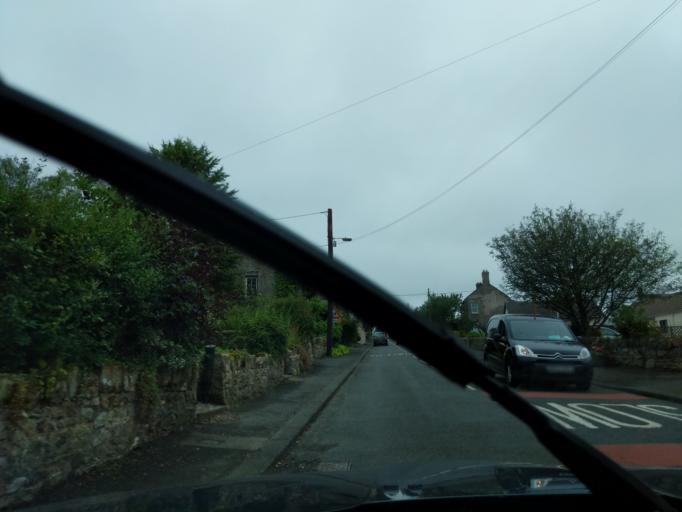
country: GB
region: England
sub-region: Northumberland
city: Lowick
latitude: 55.6514
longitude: -1.9734
